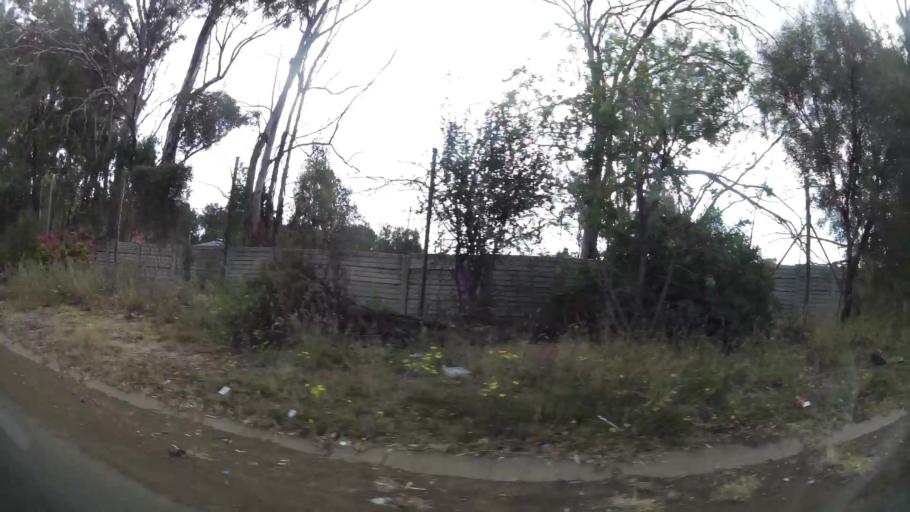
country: ZA
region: Orange Free State
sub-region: Mangaung Metropolitan Municipality
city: Bloemfontein
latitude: -29.0806
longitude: 26.1962
